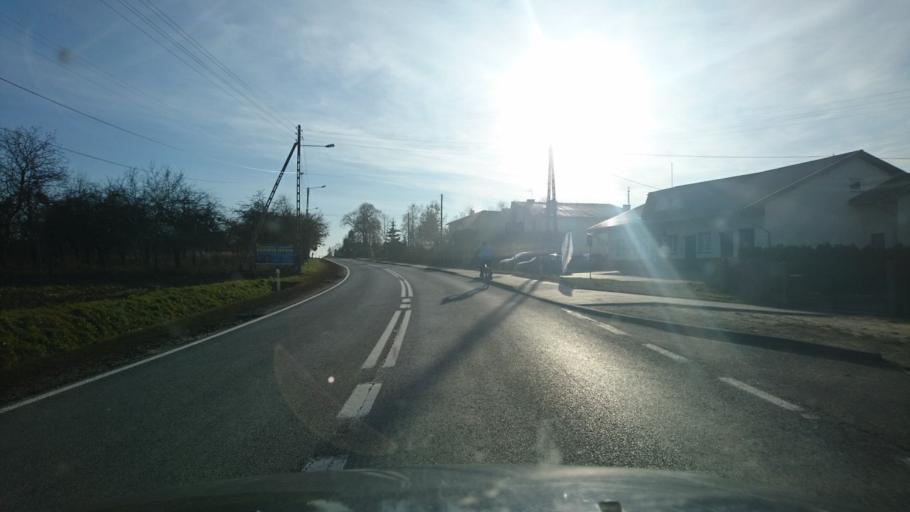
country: PL
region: Opole Voivodeship
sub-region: Powiat oleski
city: Dalachow
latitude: 51.0438
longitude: 18.5967
